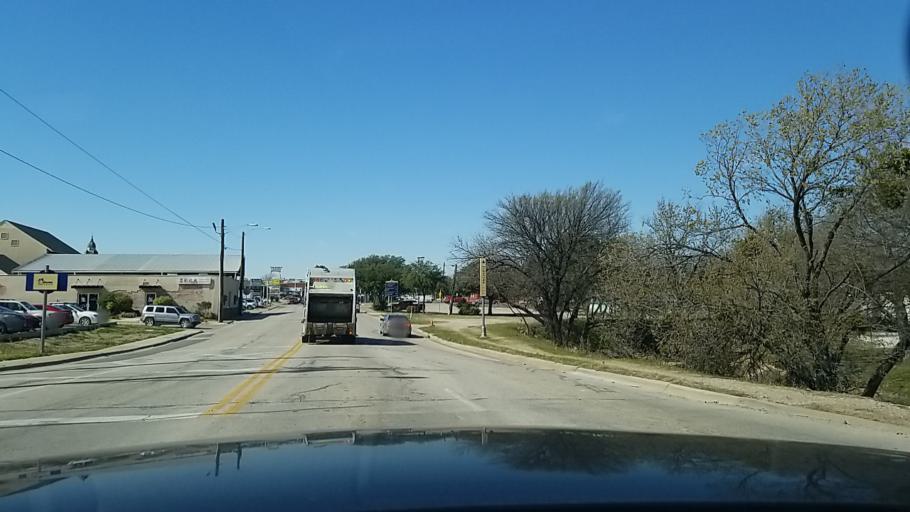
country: US
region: Texas
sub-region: Denton County
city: Denton
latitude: 33.2164
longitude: -97.1263
